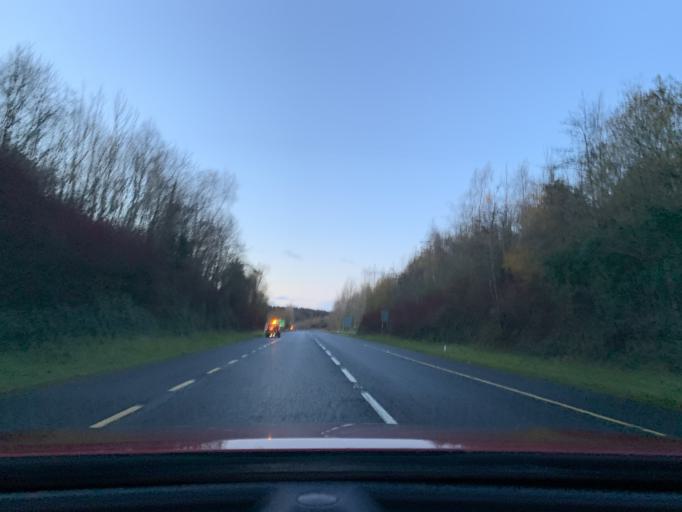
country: IE
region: Connaught
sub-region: County Leitrim
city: Carrick-on-Shannon
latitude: 53.9311
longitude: -8.0029
